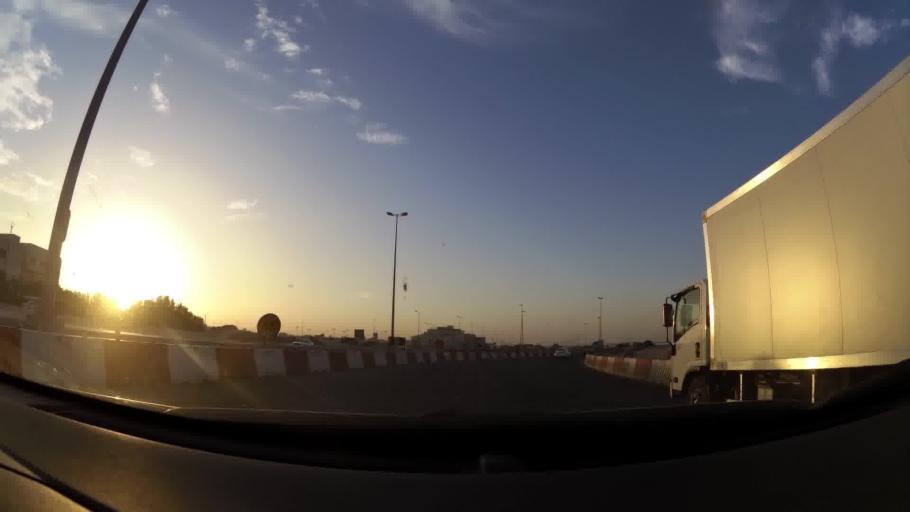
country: KW
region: Al Asimah
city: Ar Rabiyah
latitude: 29.3149
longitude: 47.8712
